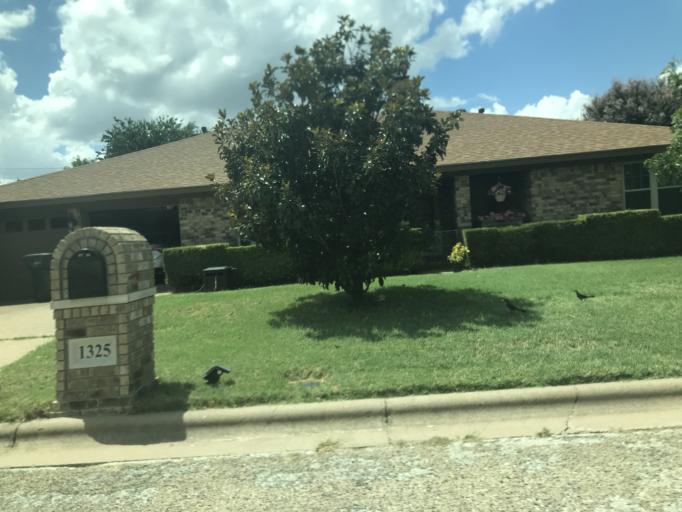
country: US
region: Texas
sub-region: Taylor County
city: Abilene
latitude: 32.4379
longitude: -99.7016
